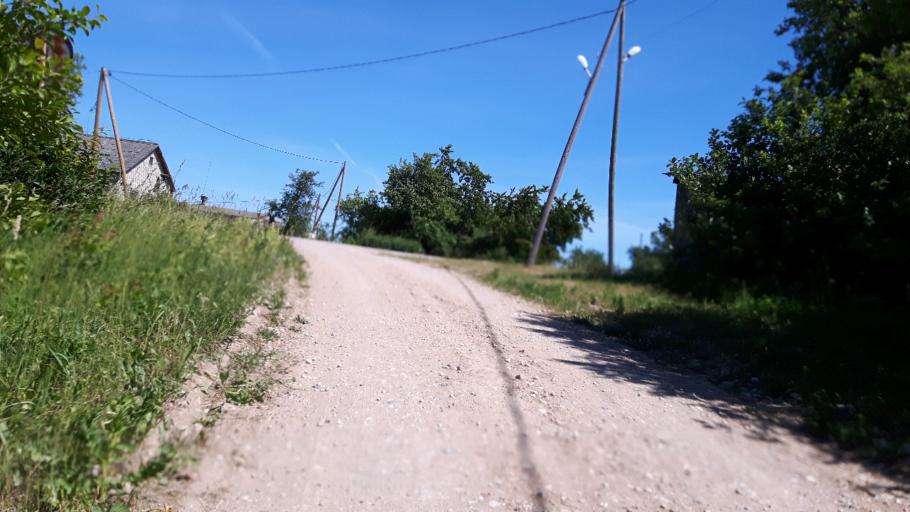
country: LV
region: Kandava
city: Kandava
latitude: 57.0381
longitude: 22.9037
